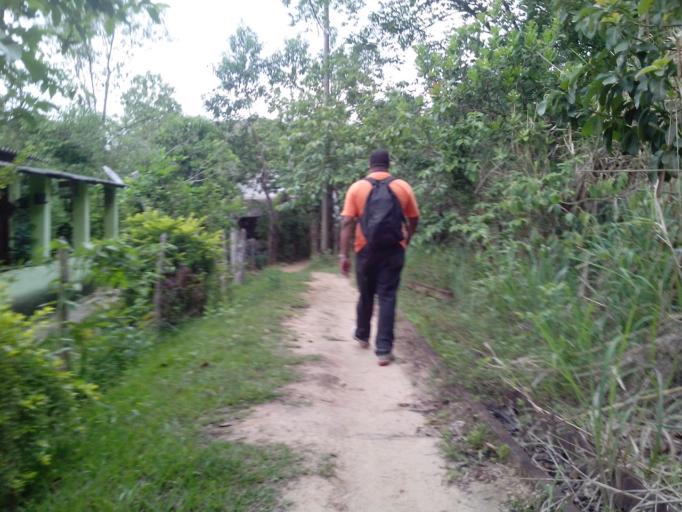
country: BR
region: Rio de Janeiro
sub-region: Miguel Pereira
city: Miguel Pereira
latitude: -22.5089
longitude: -43.5191
